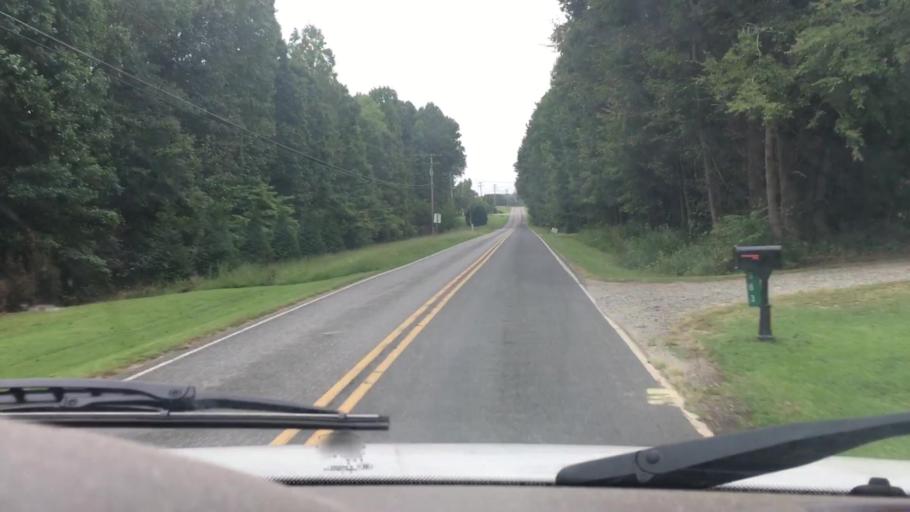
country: US
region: North Carolina
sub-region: Gaston County
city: Davidson
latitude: 35.5181
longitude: -80.8206
